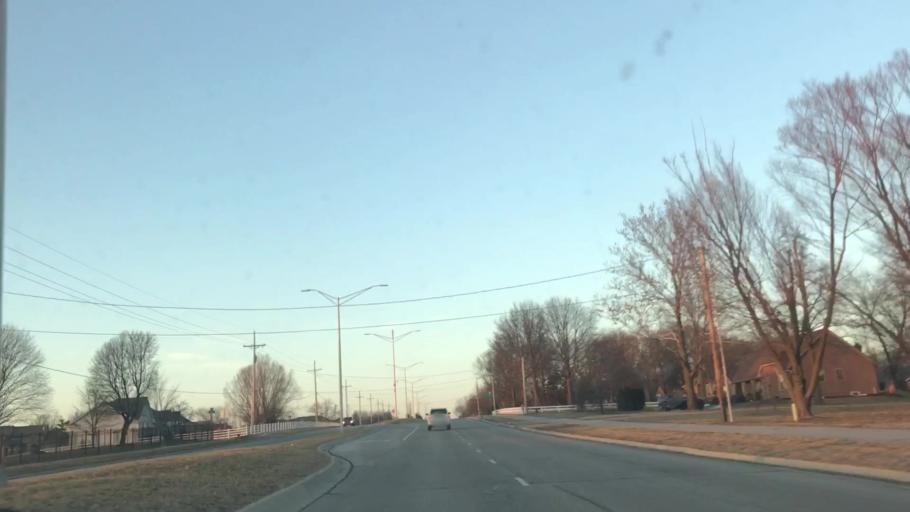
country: US
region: Kansas
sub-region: Johnson County
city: Lenexa
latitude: 38.8414
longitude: -94.7051
